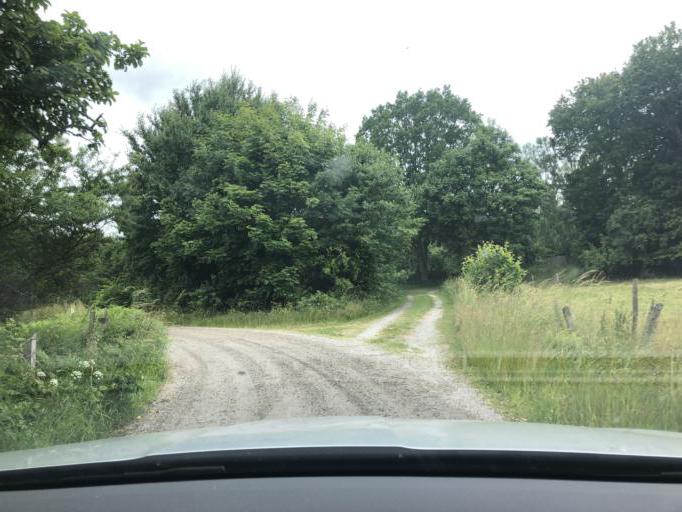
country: SE
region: Blekinge
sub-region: Solvesborgs Kommun
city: Soelvesborg
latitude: 56.1566
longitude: 14.5915
